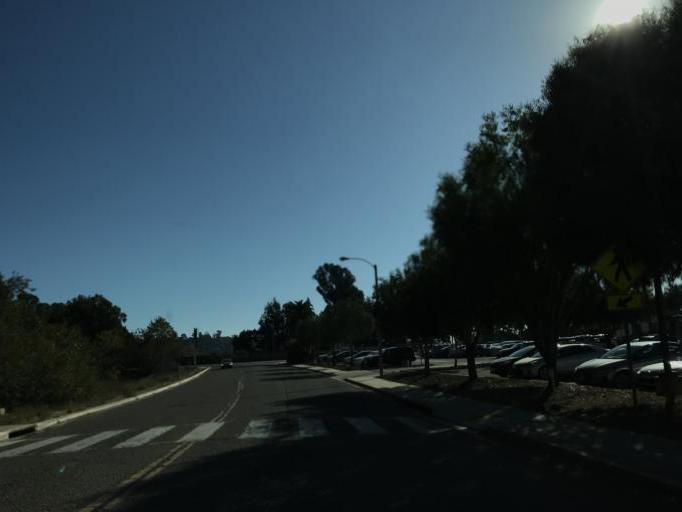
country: US
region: California
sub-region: Santa Barbara County
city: Goleta
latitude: 34.4435
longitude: -119.7795
